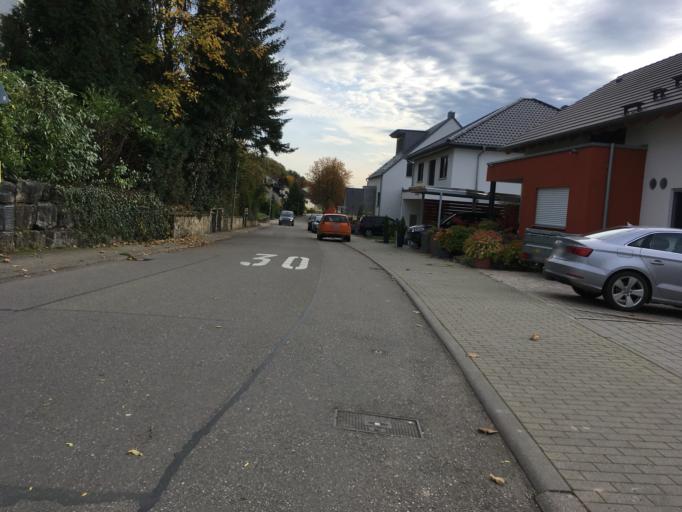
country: DE
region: Baden-Wuerttemberg
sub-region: Karlsruhe Region
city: Sinsheim
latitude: 49.2574
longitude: 8.9045
